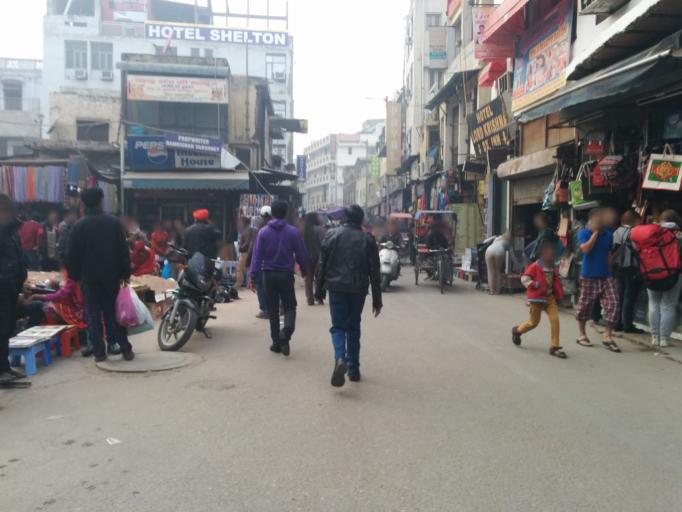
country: IN
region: NCT
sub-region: New Delhi
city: New Delhi
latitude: 28.6411
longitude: 77.2137
